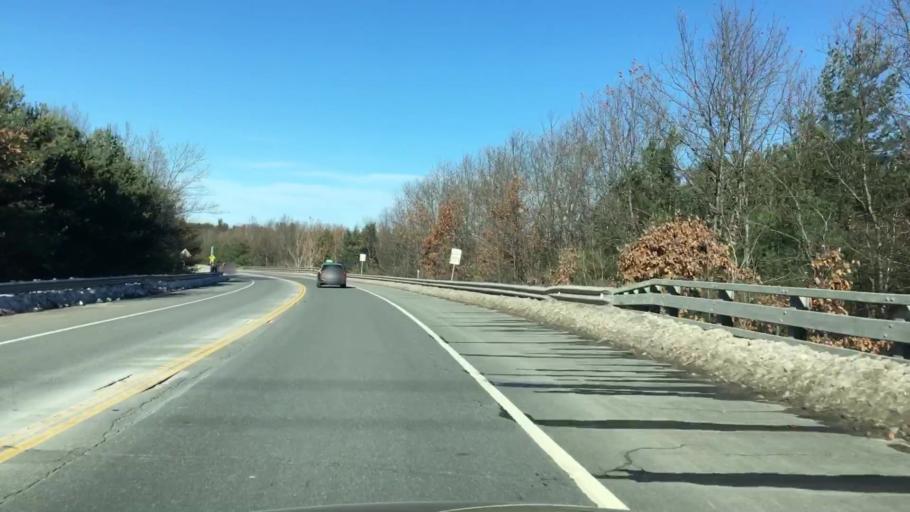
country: US
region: New Hampshire
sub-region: Hillsborough County
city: Milford
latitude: 42.8256
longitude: -71.6170
